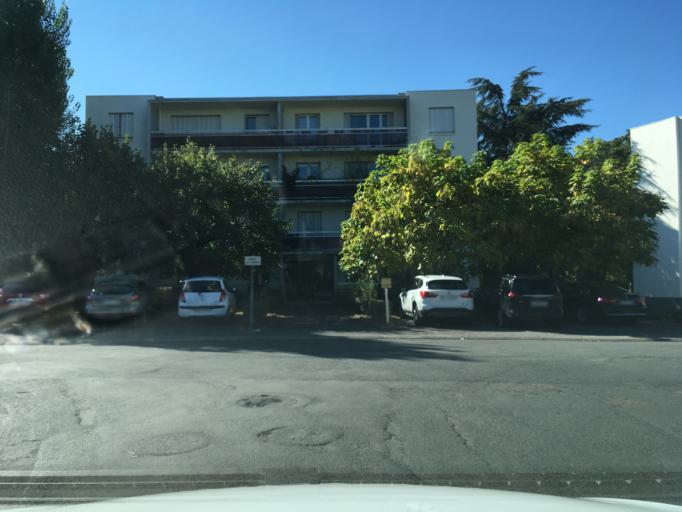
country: FR
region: Limousin
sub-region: Departement de la Correze
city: Ussac
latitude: 45.1599
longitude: 1.4959
